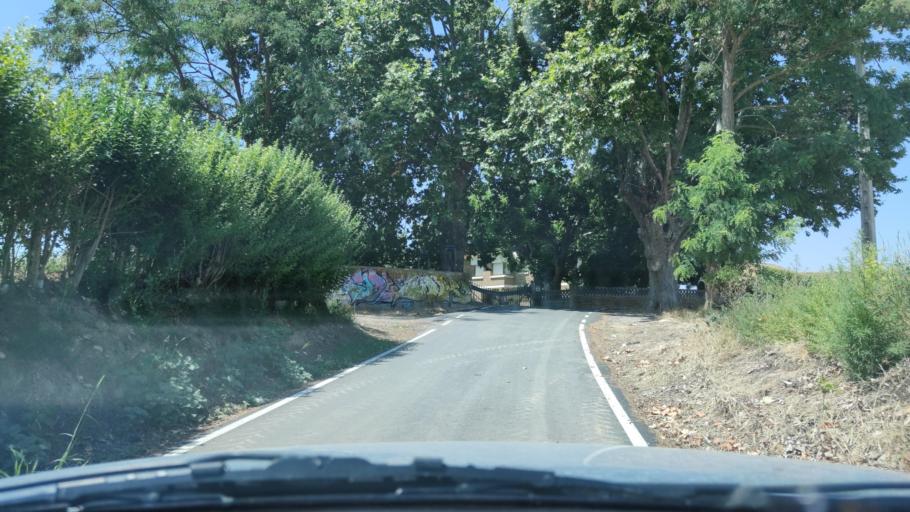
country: ES
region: Catalonia
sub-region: Provincia de Lleida
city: Alpicat
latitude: 41.6527
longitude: 0.5664
